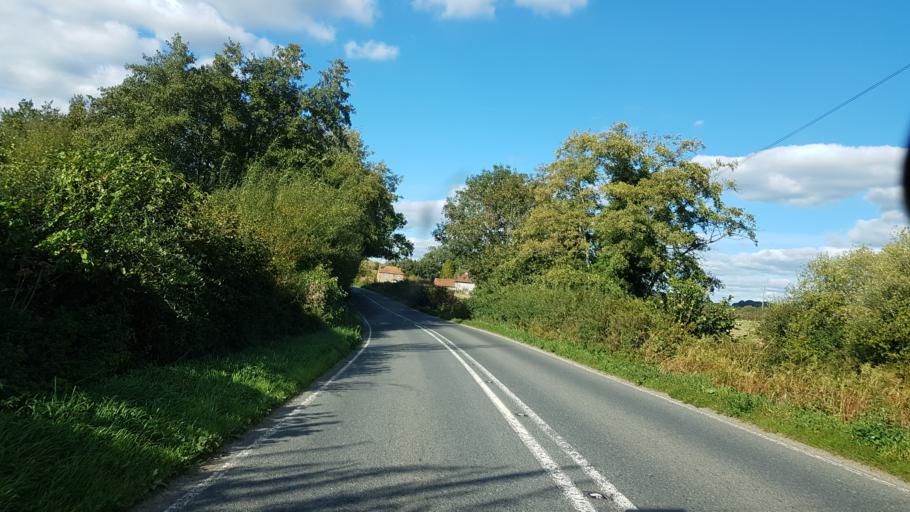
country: GB
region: England
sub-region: Surrey
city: Chiddingfold
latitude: 51.0714
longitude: -0.6445
